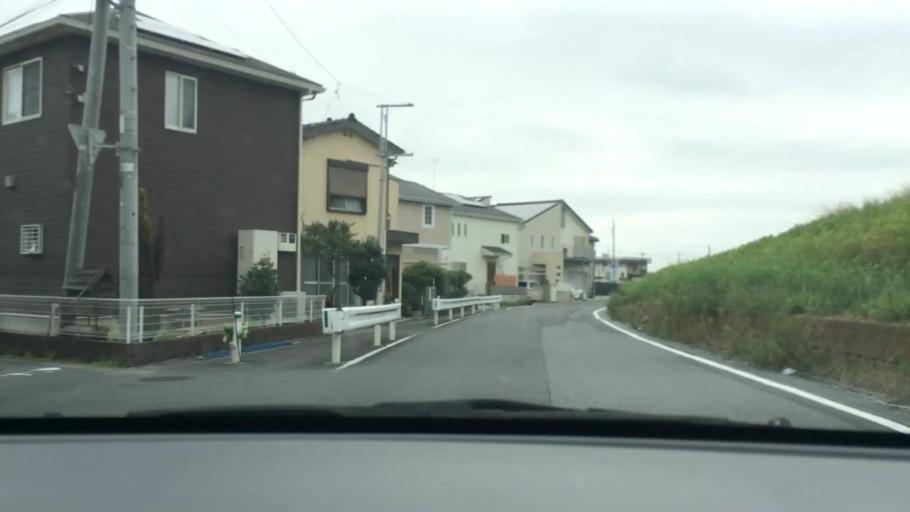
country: JP
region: Chiba
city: Matsudo
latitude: 35.8059
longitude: 139.8850
